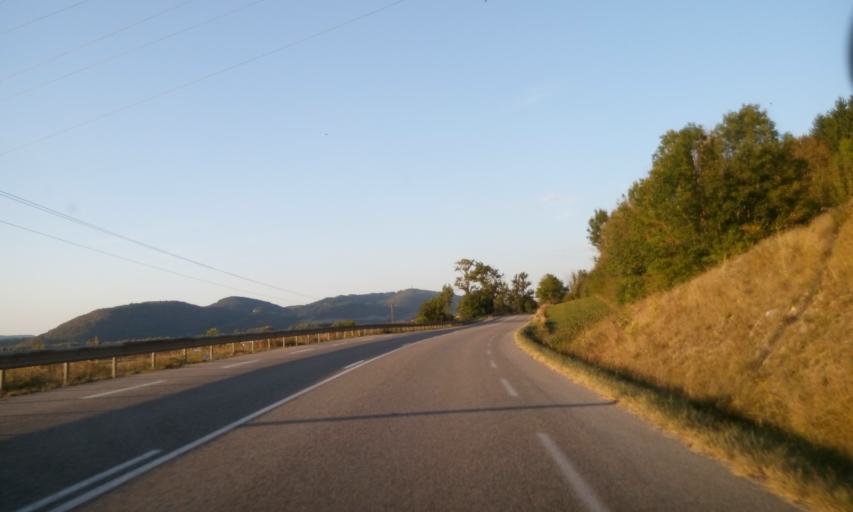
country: FR
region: Rhone-Alpes
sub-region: Departement de l'Ain
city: Saint-Martin-du-Frene
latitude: 46.1538
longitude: 5.5638
